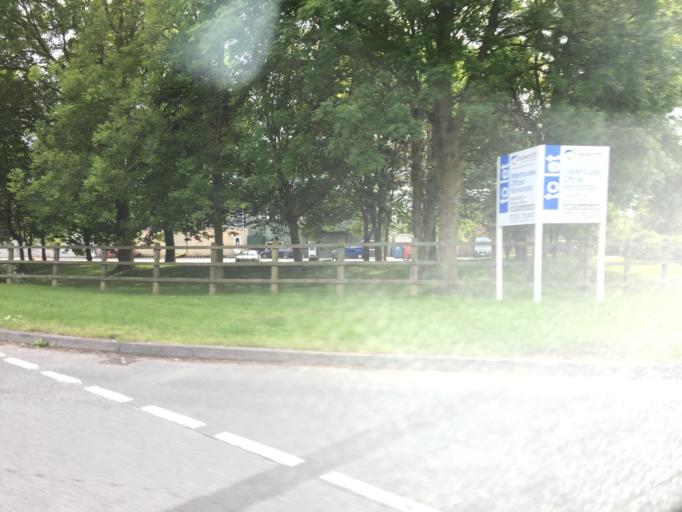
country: GB
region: England
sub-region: Wiltshire
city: Cricklade
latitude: 51.6310
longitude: -1.8784
